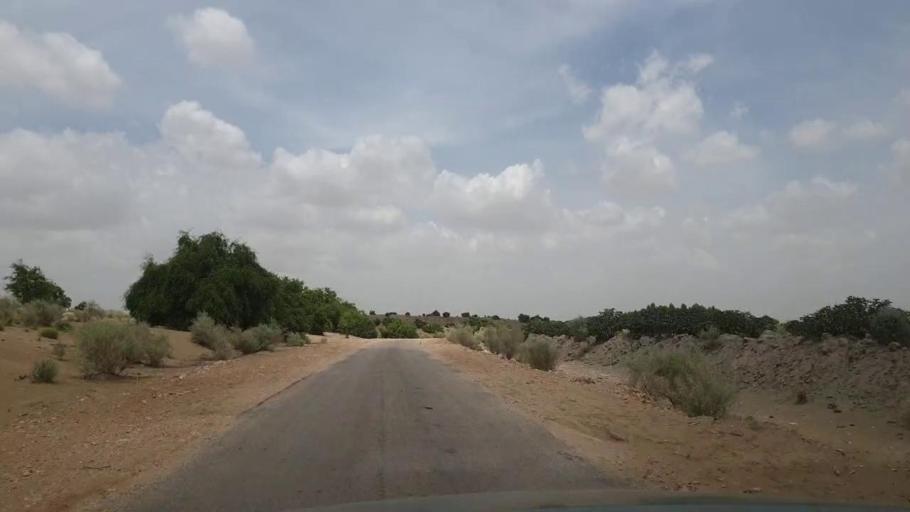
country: PK
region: Sindh
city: Kot Diji
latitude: 27.2019
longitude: 69.0829
